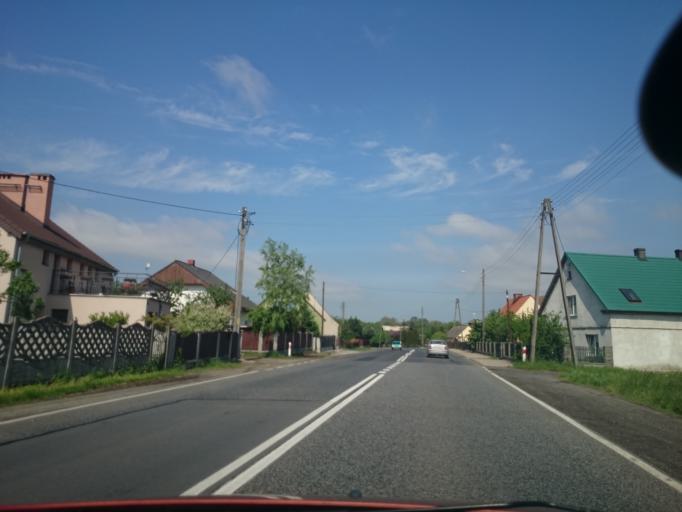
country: PL
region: Opole Voivodeship
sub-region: Powiat opolski
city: Dabrowa
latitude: 50.7198
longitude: 17.7689
